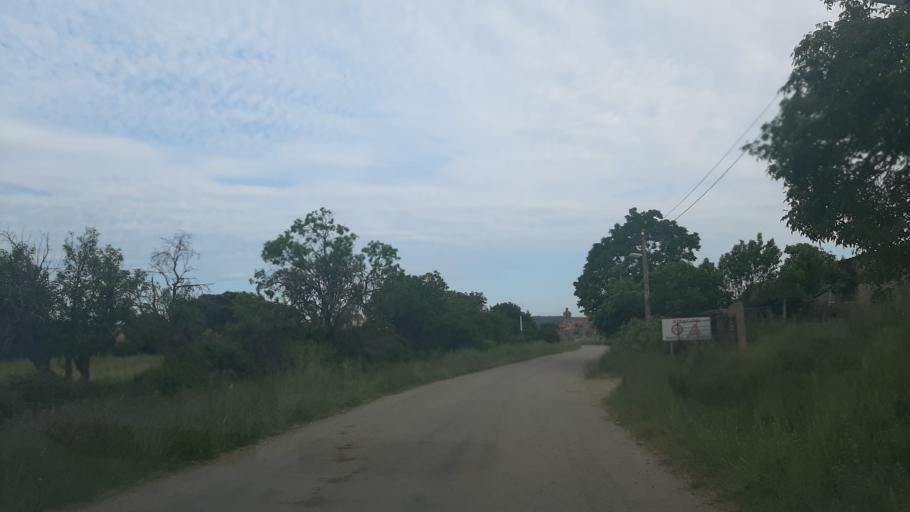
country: ES
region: Castille and Leon
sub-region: Provincia de Salamanca
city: Gallegos de Arganan
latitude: 40.6476
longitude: -6.7544
